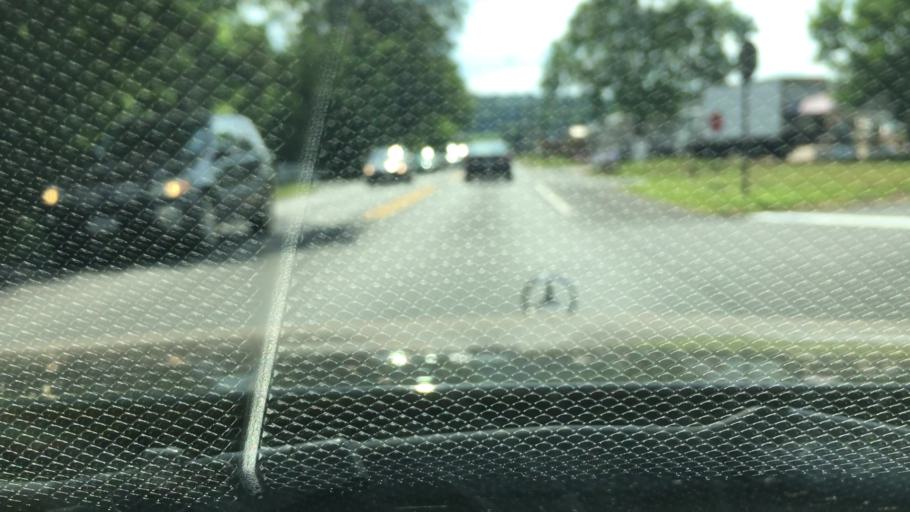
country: US
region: Virginia
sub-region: Orange County
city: Orange
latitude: 38.2410
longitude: -78.1043
